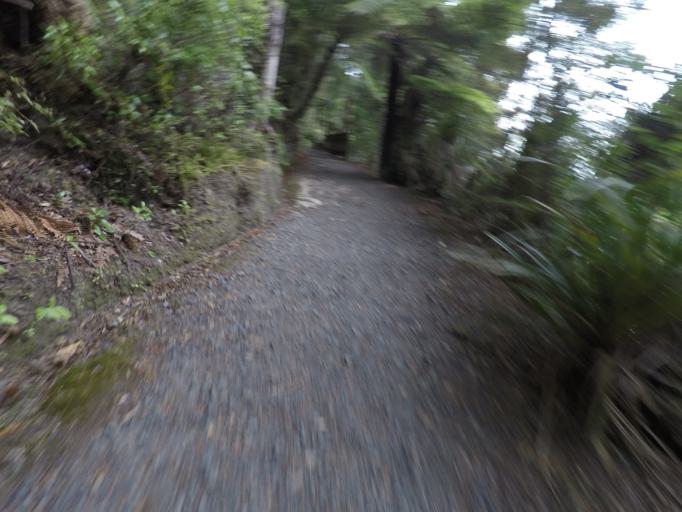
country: NZ
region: Northland
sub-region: Whangarei
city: Whangarei
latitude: -35.7124
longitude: 174.3305
